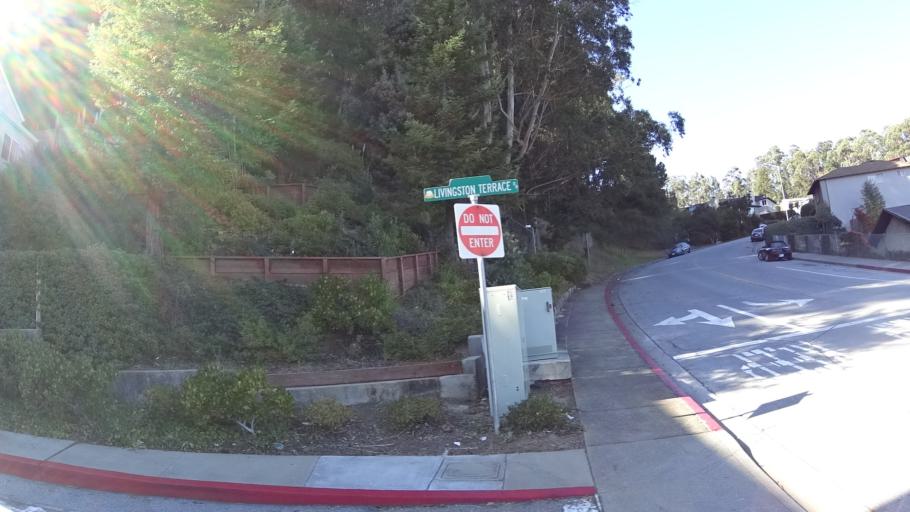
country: US
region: California
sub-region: San Mateo County
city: San Bruno
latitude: 37.6235
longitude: -122.4294
